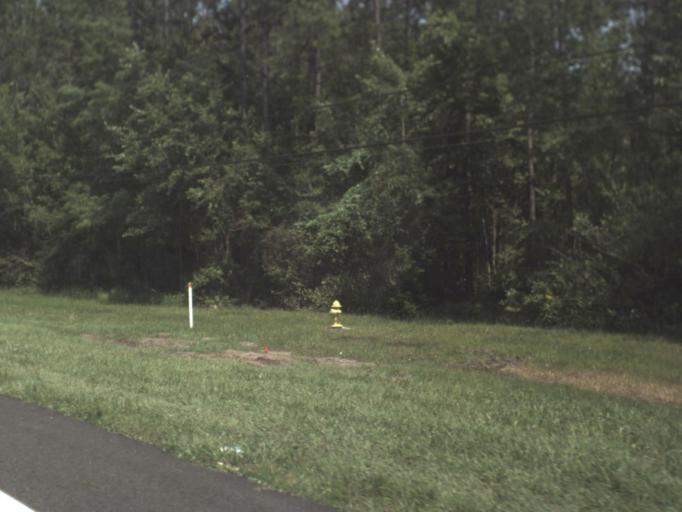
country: US
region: Florida
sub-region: Duval County
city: Baldwin
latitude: 30.2661
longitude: -81.8512
